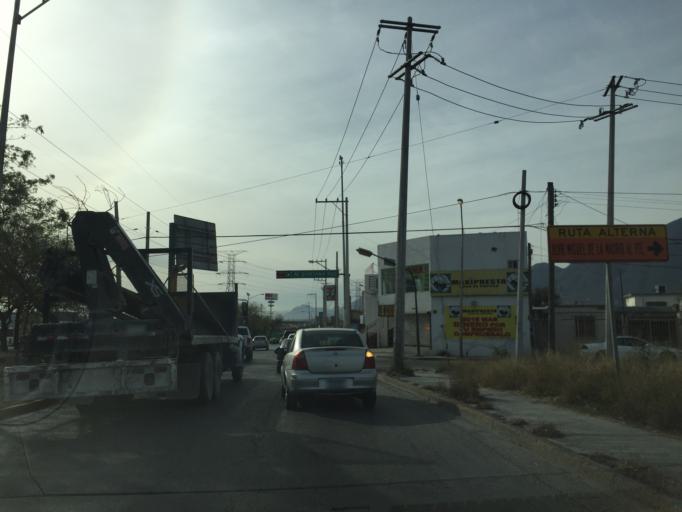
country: MX
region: Nuevo Leon
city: Guadalupe
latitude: 25.6971
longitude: -100.2131
